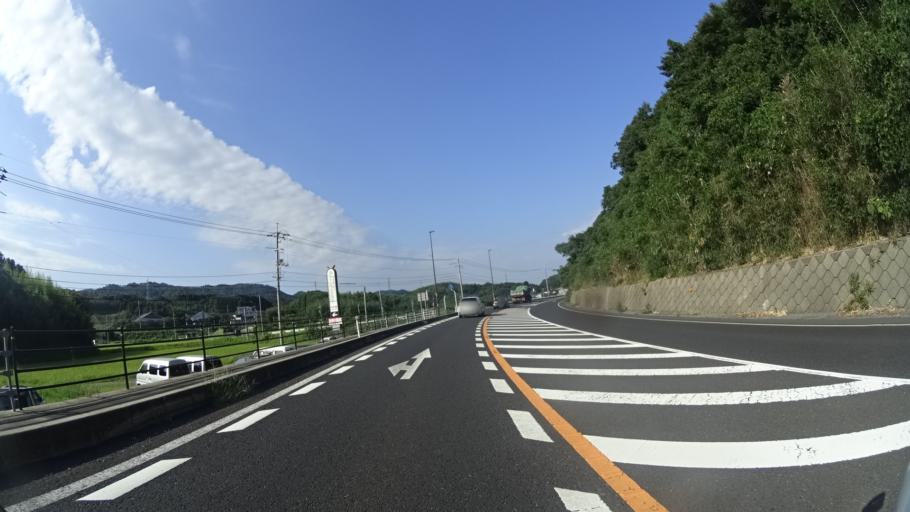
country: JP
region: Shimane
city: Izumo
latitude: 35.2961
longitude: 132.6478
